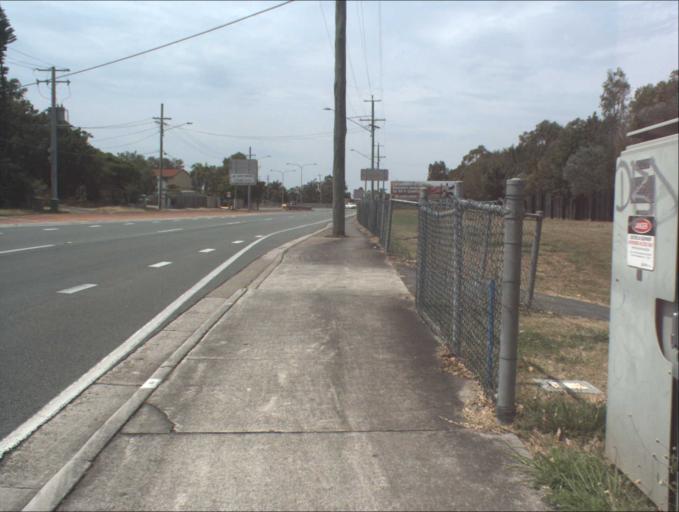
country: AU
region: Queensland
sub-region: Logan
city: Rochedale South
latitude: -27.5941
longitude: 153.1076
